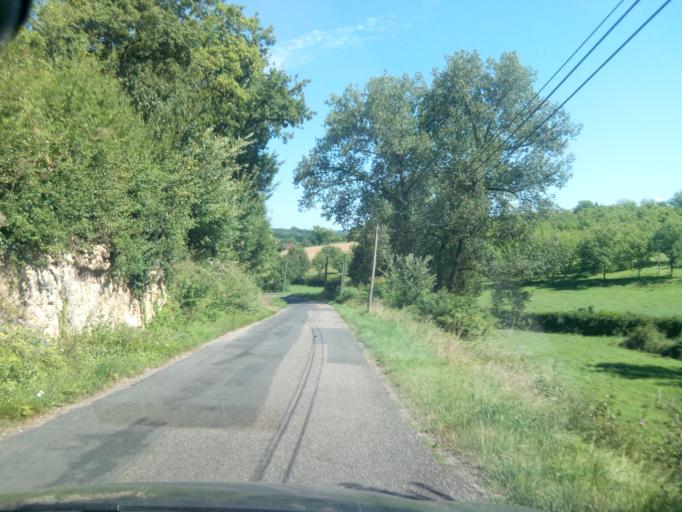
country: FR
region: Midi-Pyrenees
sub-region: Departement du Lot
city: Vayrac
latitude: 45.0098
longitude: 1.7134
